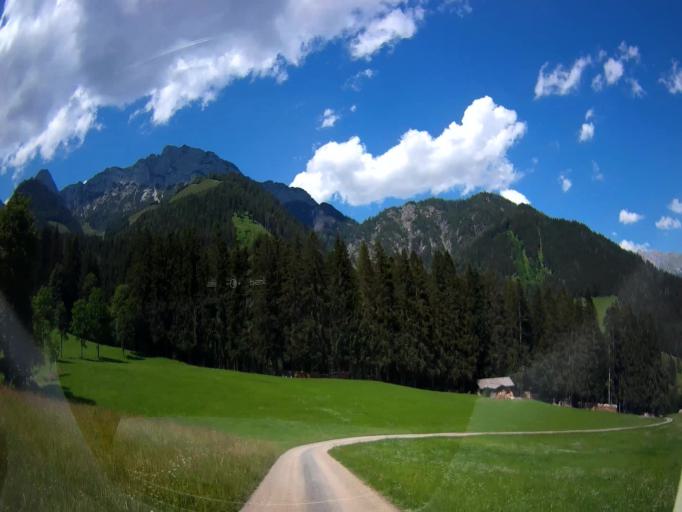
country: AT
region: Salzburg
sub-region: Politischer Bezirk Zell am See
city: Leogang
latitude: 47.4501
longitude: 12.7868
